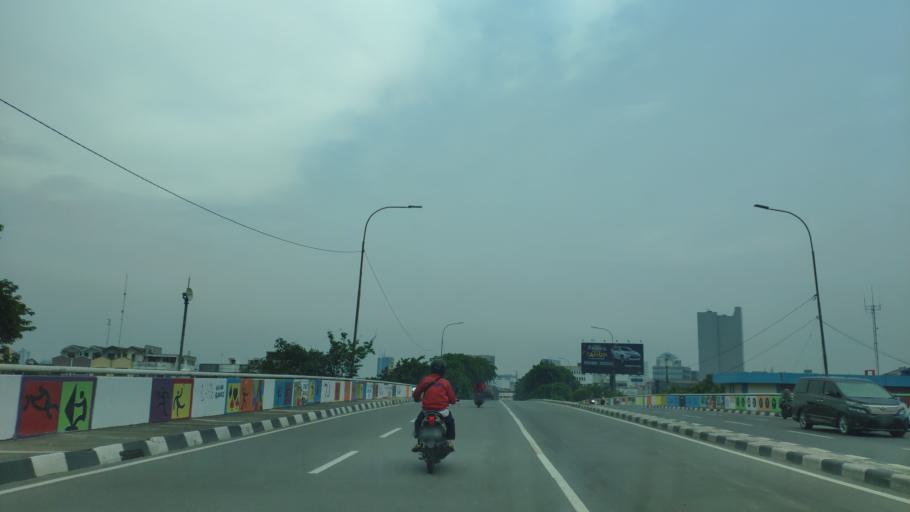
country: ID
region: Jakarta Raya
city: Jakarta
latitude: -6.1738
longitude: 106.8051
